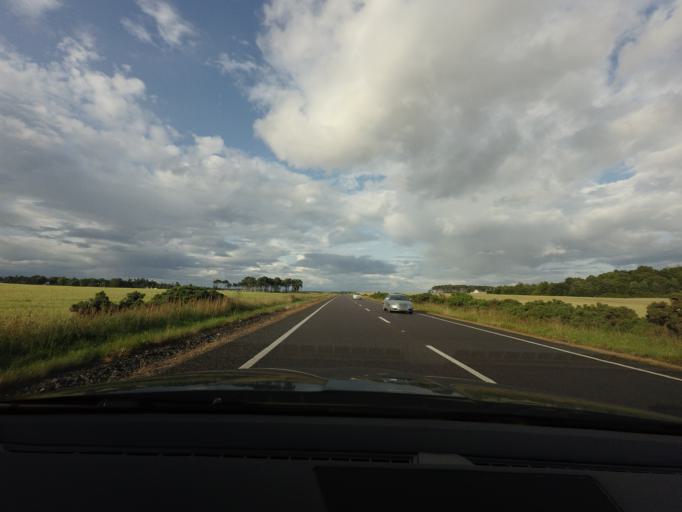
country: GB
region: Scotland
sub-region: Highland
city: Nairn
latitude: 57.5481
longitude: -3.9949
